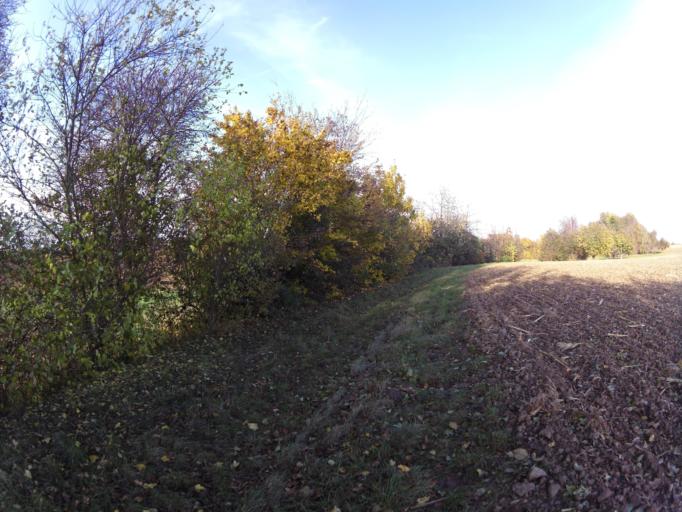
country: DE
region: Bavaria
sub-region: Regierungsbezirk Unterfranken
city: Giebelstadt
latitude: 49.6667
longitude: 9.9581
